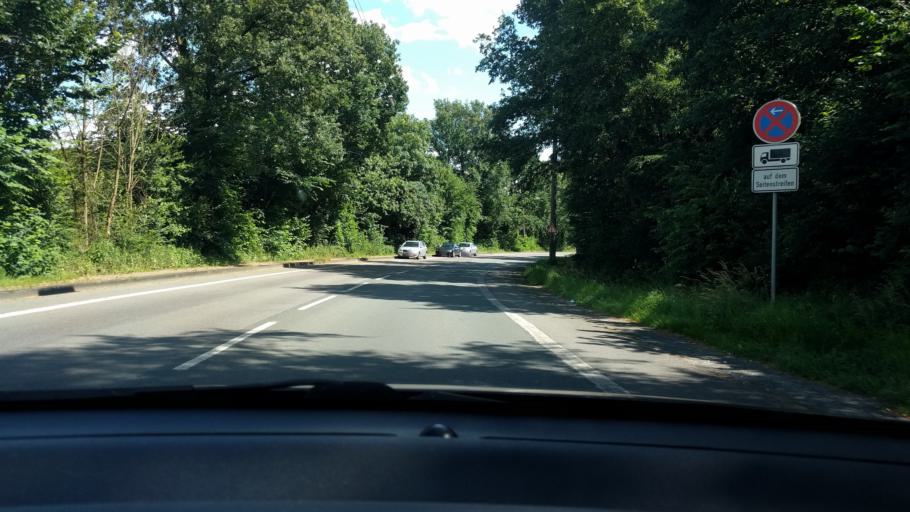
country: DE
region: North Rhine-Westphalia
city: Datteln
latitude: 51.6589
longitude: 7.3362
